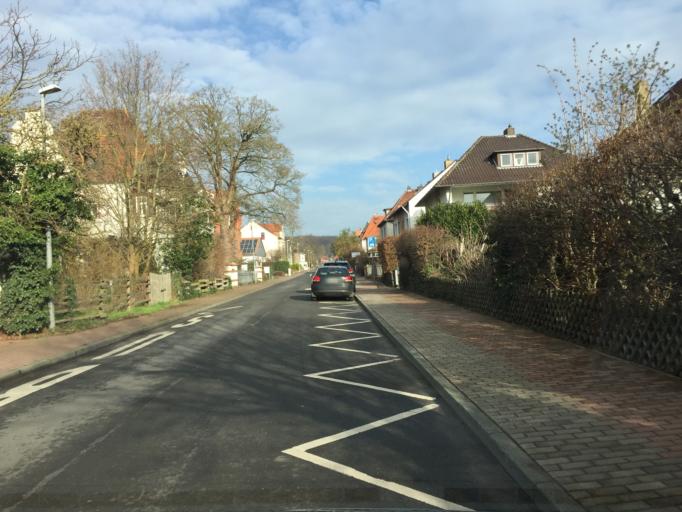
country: DE
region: Lower Saxony
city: Ronnenberg
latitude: 52.3310
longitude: 9.6305
